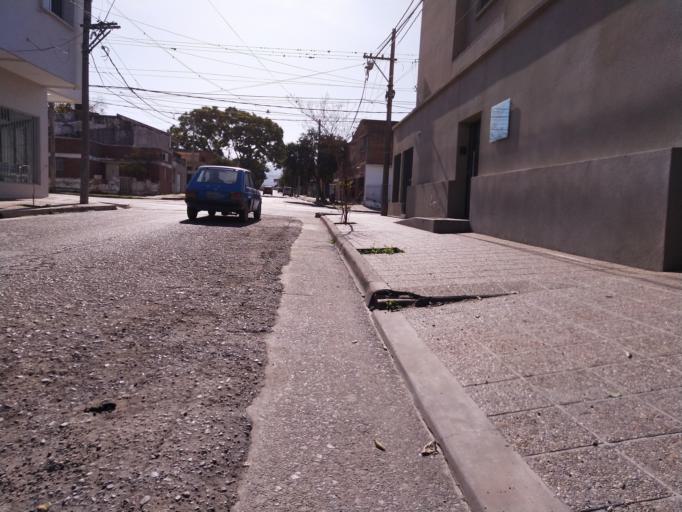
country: AR
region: Jujuy
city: San Salvador de Jujuy
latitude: -24.1999
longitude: -65.2868
